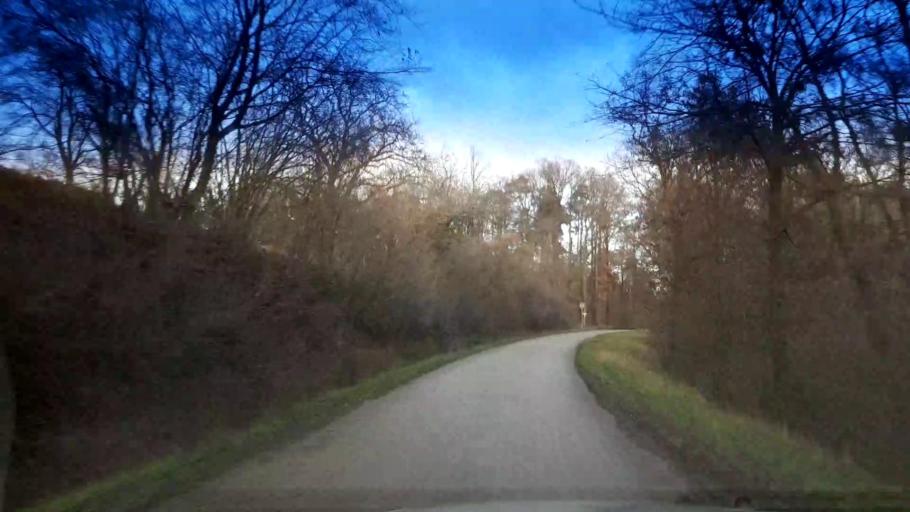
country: DE
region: Bavaria
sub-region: Regierungsbezirk Unterfranken
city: Stettfeld
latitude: 49.9726
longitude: 10.7393
